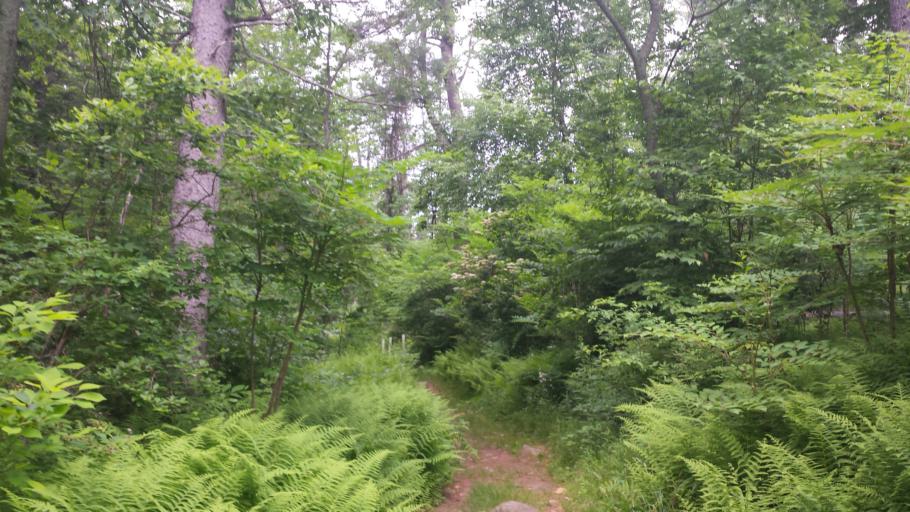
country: US
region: New York
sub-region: Westchester County
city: Pound Ridge
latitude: 41.2628
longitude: -73.5958
